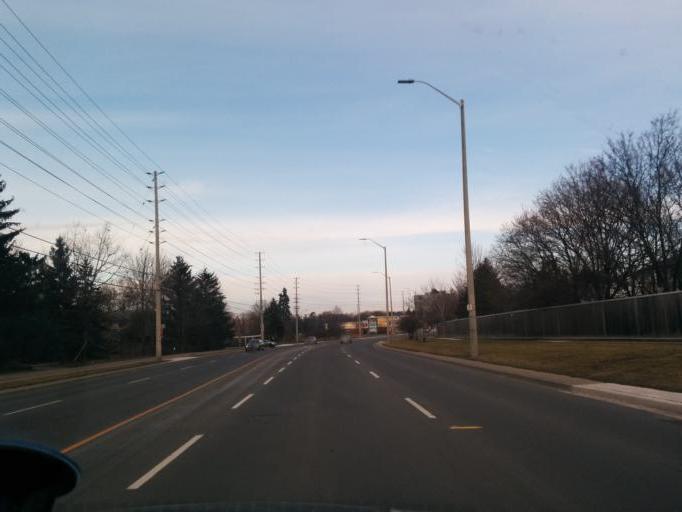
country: CA
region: Ontario
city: Mississauga
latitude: 43.5412
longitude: -79.6946
